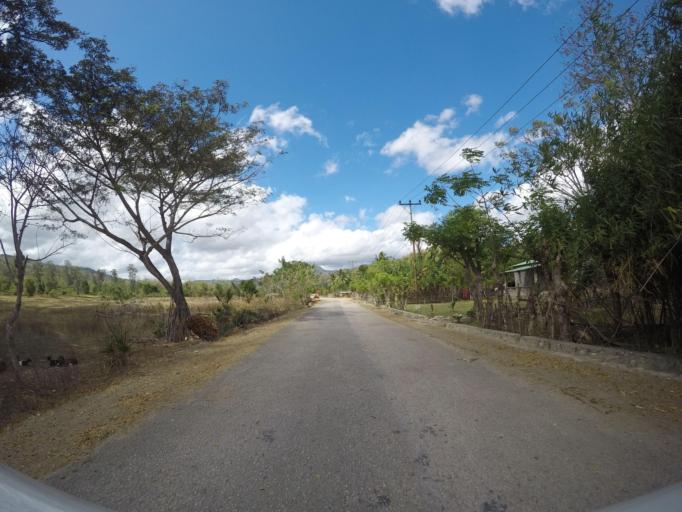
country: TL
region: Lautem
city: Lospalos
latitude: -8.4712
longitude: 126.8173
